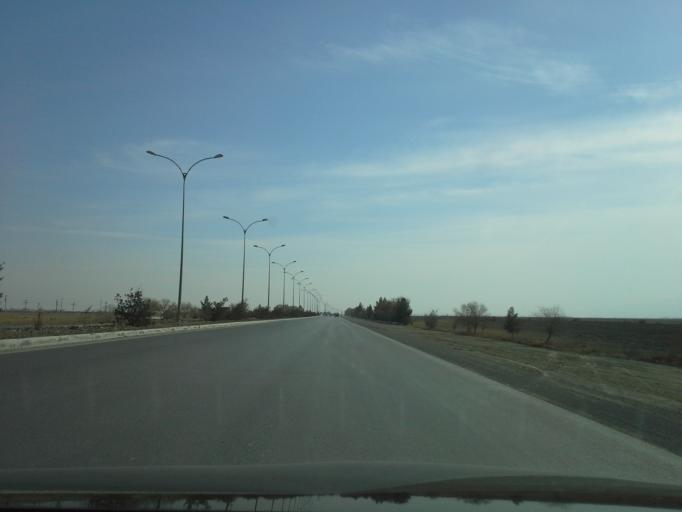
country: TM
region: Ahal
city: Abadan
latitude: 38.1275
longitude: 58.0292
